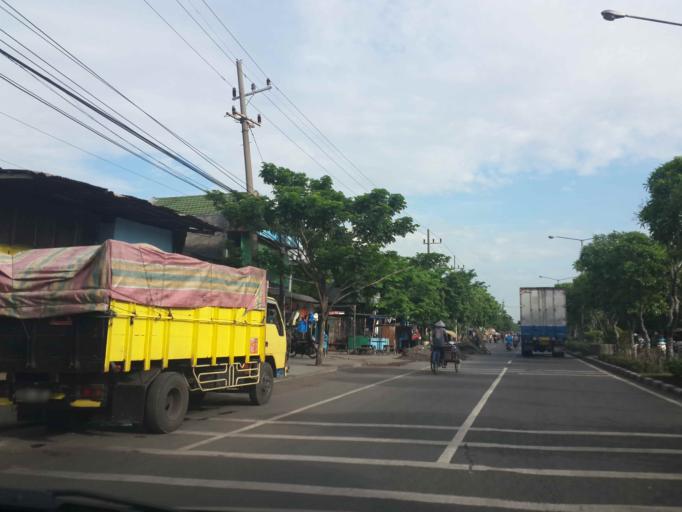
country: ID
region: East Java
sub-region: Kota Surabaya
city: Surabaya
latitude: -7.2444
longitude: 112.7209
